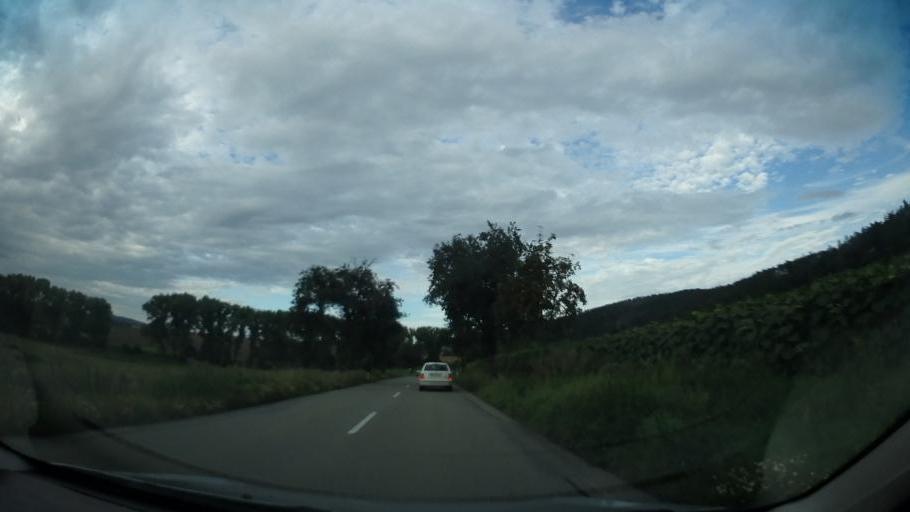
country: CZ
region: South Moravian
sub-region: Okres Blansko
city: Boskovice
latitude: 49.5122
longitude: 16.6755
